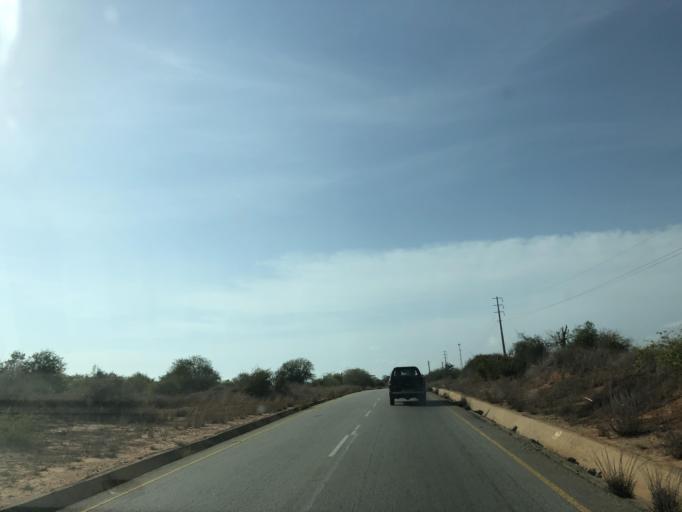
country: AO
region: Luanda
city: Luanda
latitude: -9.2639
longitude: 13.1207
